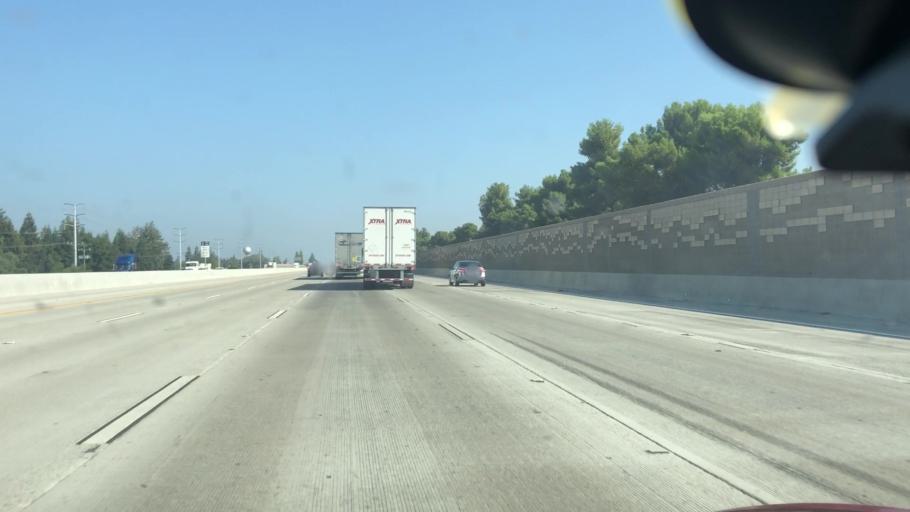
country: US
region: California
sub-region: San Joaquin County
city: Lincoln Village
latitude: 37.9936
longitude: -121.3468
